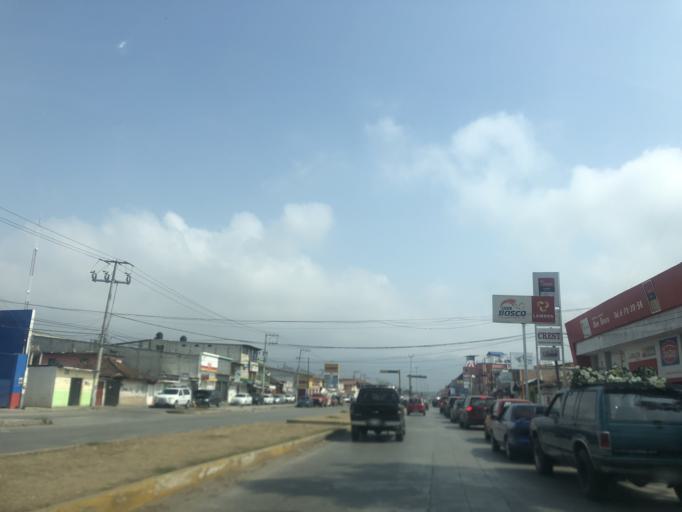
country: MX
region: Chiapas
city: San Cristobal de las Casas
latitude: 16.7175
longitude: -92.6369
